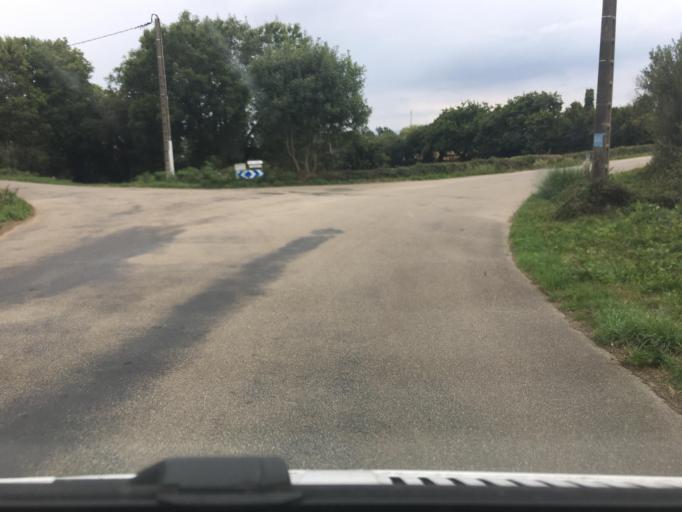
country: FR
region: Brittany
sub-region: Departement du Finistere
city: Beuzec-Cap-Sizun
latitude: 48.0796
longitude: -4.4777
